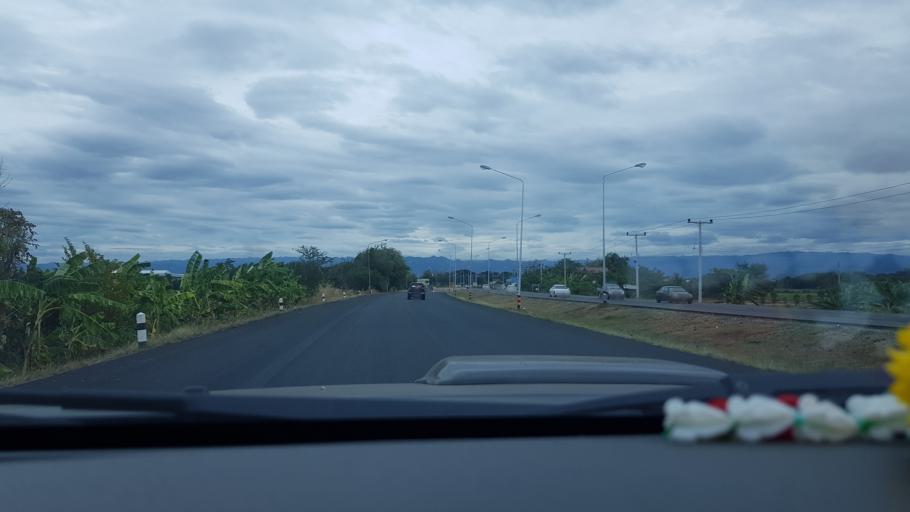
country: TH
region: Phetchabun
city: Phetchabun
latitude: 16.4971
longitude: 101.1519
